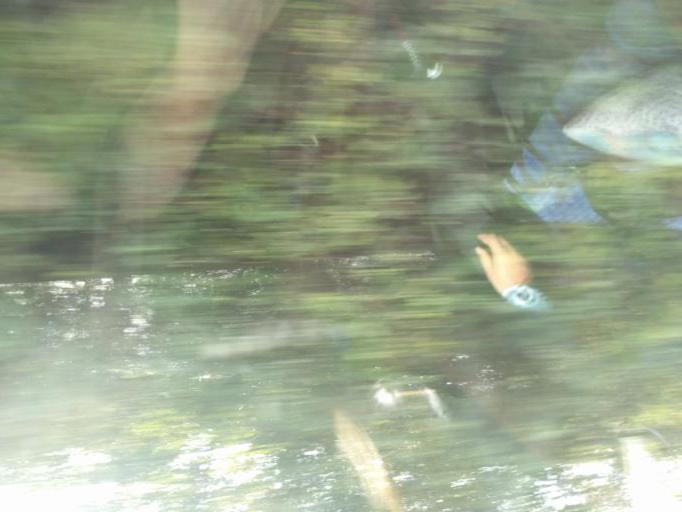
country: DE
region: Schleswig-Holstein
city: Heidekamp
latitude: 53.8393
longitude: 10.5191
